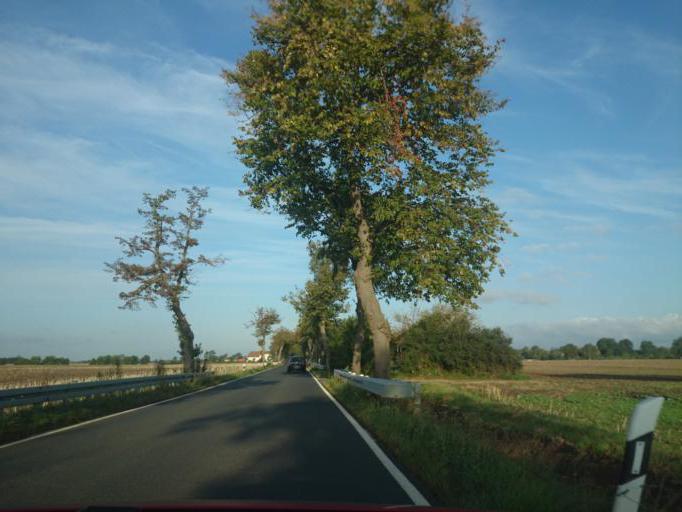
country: DE
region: Mecklenburg-Vorpommern
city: Velgast
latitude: 54.3317
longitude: 12.8528
